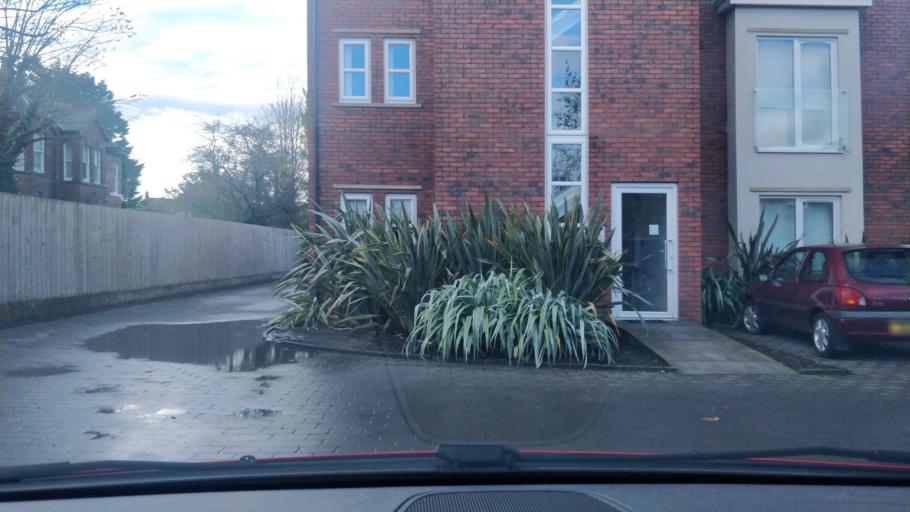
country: GB
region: England
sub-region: Sefton
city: Southport
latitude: 53.6322
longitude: -3.0158
